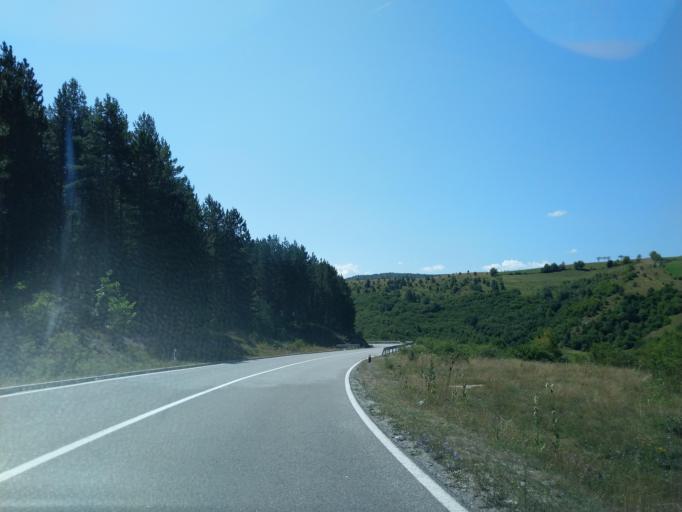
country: RS
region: Central Serbia
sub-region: Zlatiborski Okrug
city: Sjenica
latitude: 43.3040
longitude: 19.9296
